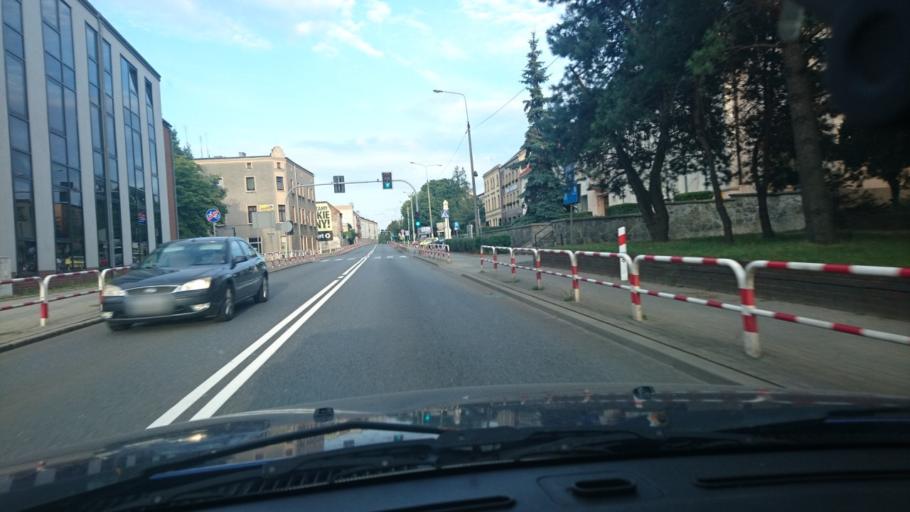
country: PL
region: Opole Voivodeship
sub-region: Powiat oleski
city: Olesno
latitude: 50.8748
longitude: 18.4202
